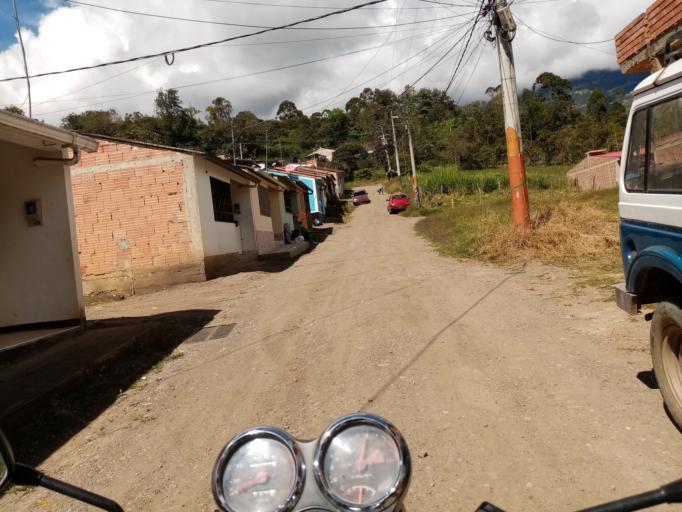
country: CO
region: Cundinamarca
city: Tenza
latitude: 5.0939
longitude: -73.4451
